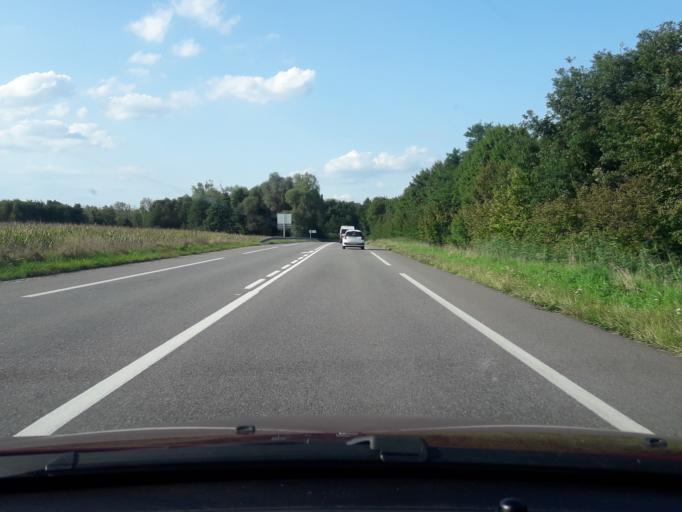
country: FR
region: Alsace
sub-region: Departement du Bas-Rhin
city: Wissembourg
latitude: 48.9641
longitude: 7.9527
